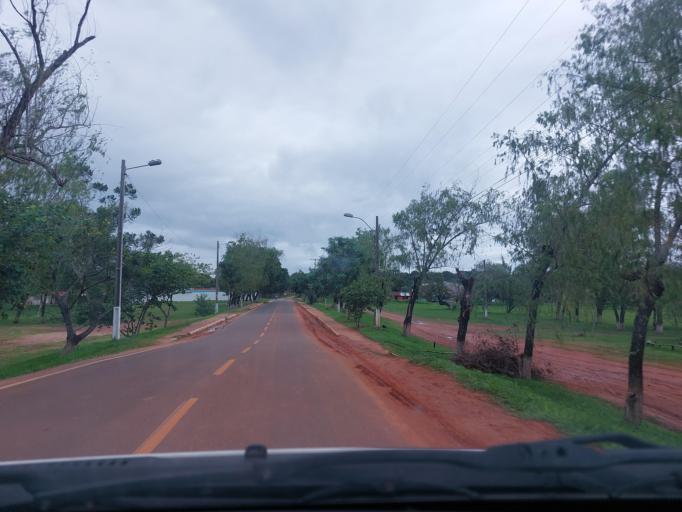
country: PY
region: San Pedro
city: Guayaybi
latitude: -24.6541
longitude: -56.4371
